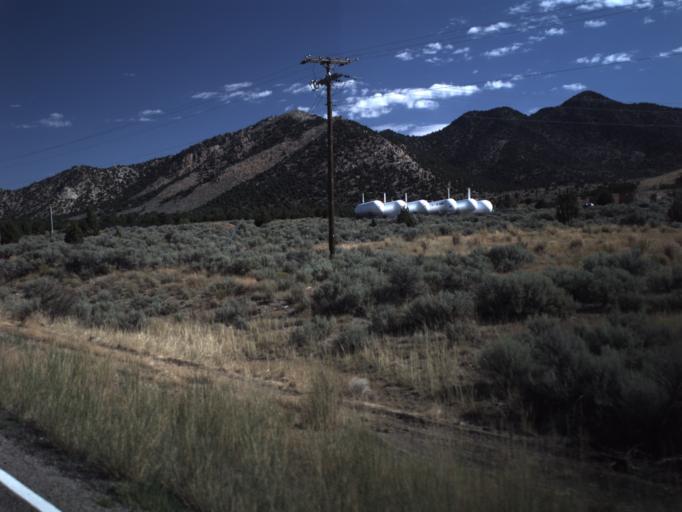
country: US
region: Utah
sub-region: Juab County
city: Mona
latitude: 39.9147
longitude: -112.1426
